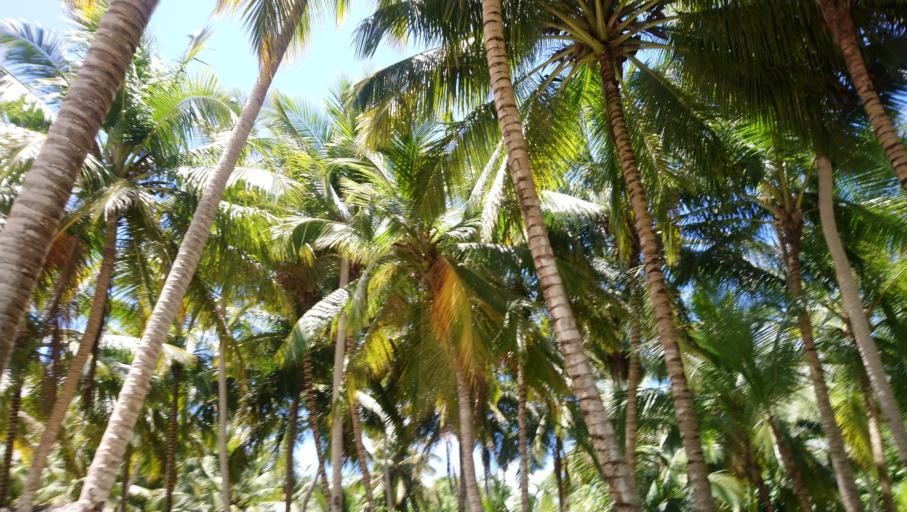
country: DO
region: La Altagracia
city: Boca de Yuma
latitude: 18.1717
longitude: -68.7808
